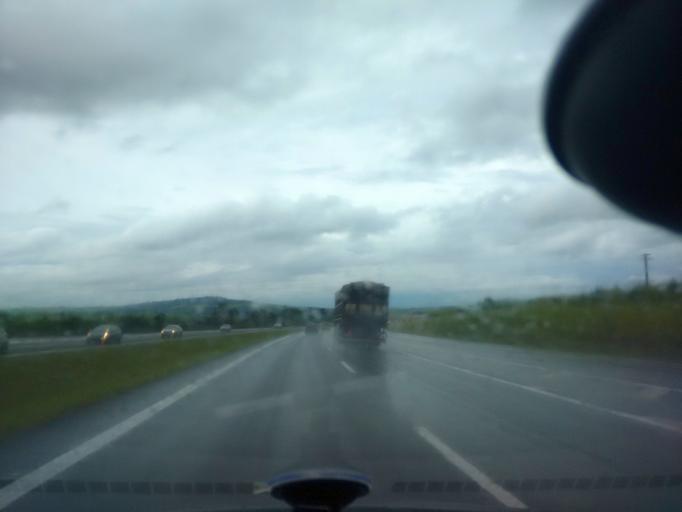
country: BR
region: Sao Paulo
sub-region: Iracemapolis
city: Iracemapolis
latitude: -22.5798
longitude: -47.4595
